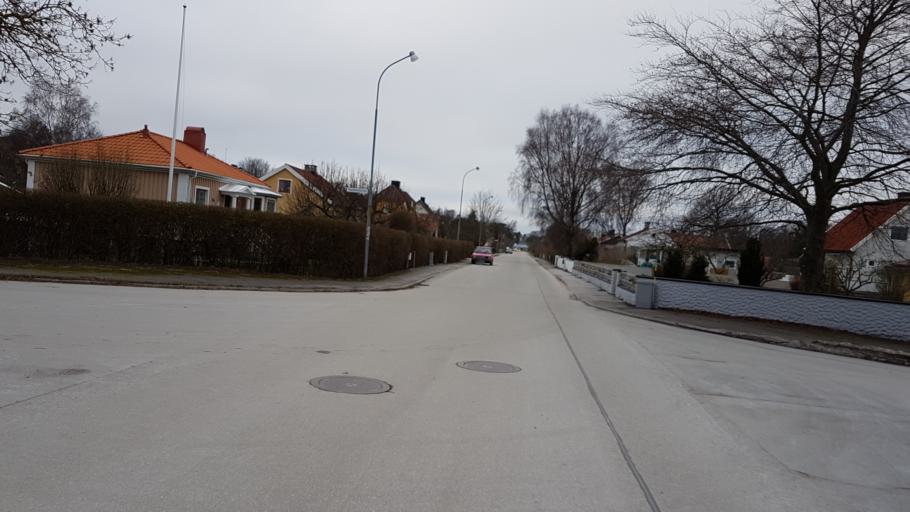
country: SE
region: Gotland
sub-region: Gotland
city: Visby
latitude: 57.6222
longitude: 18.3066
